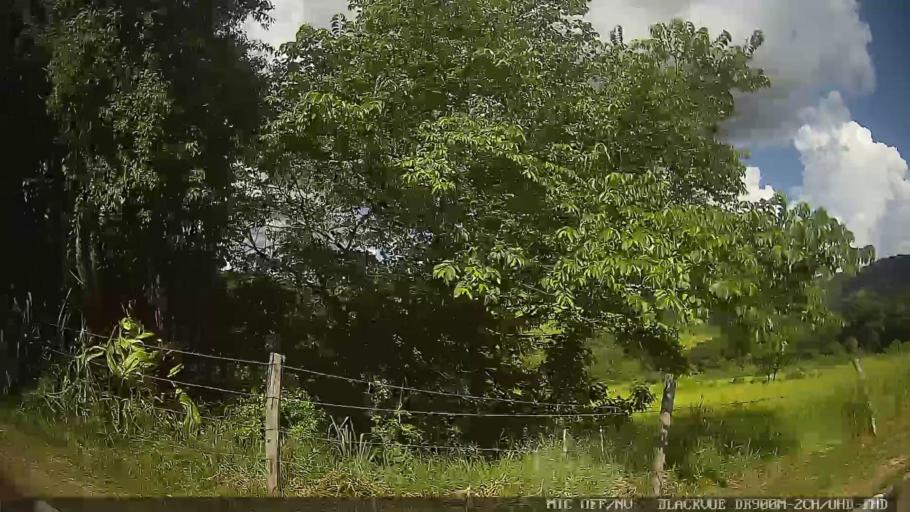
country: BR
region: Sao Paulo
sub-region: Atibaia
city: Atibaia
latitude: -23.1370
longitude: -46.5481
